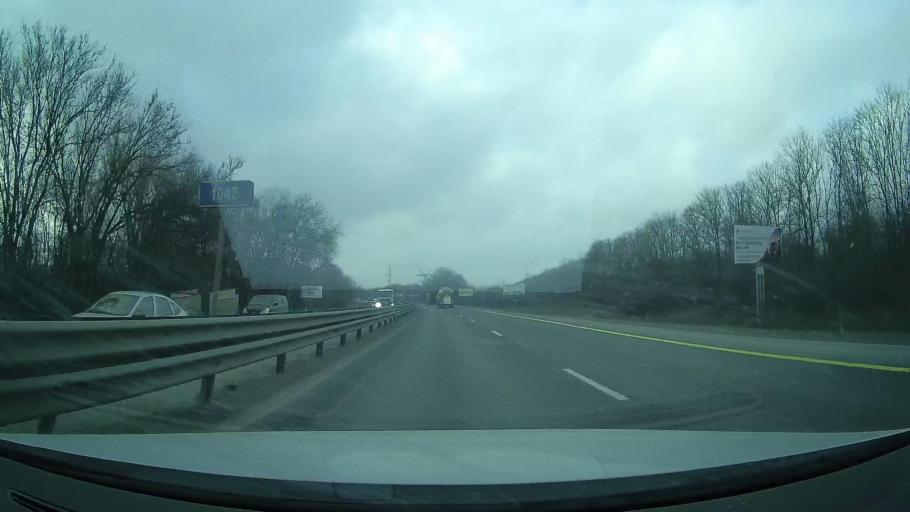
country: RU
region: Rostov
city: Grushevskaya
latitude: 47.3957
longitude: 39.9268
